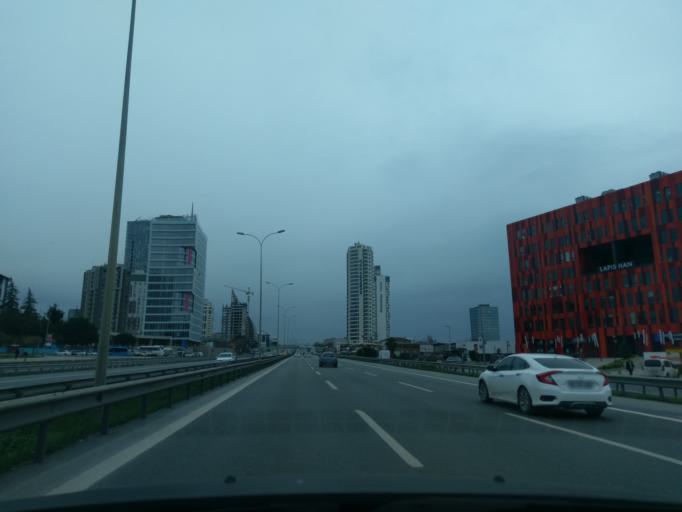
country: TR
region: Istanbul
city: Maltepe
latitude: 40.9125
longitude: 29.1921
